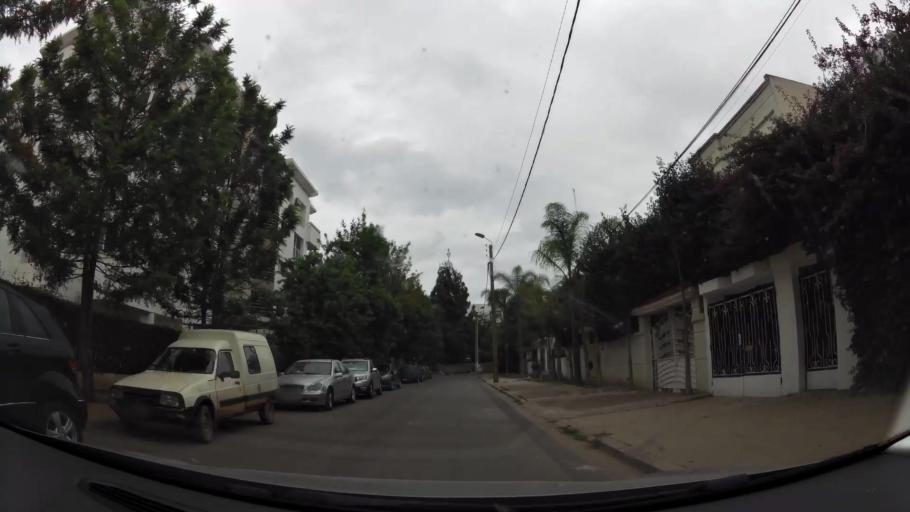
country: MA
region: Rabat-Sale-Zemmour-Zaer
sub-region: Rabat
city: Rabat
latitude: 33.9688
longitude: -6.8216
